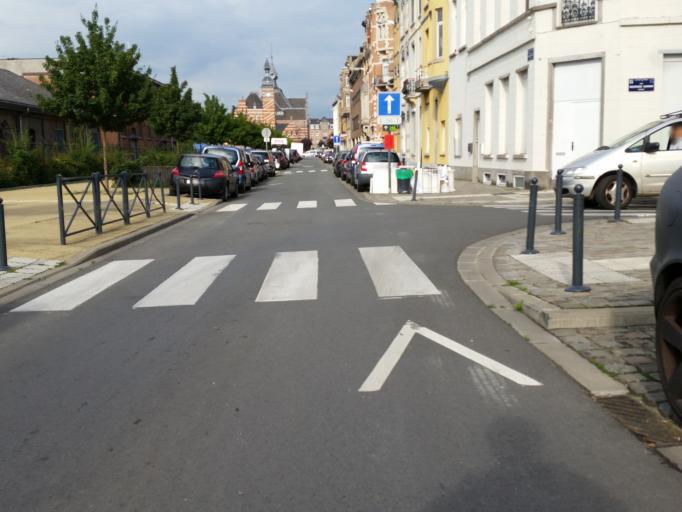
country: BE
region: Brussels Capital
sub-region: Bruxelles-Capitale
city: Brussels
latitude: 50.8764
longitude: 4.3767
